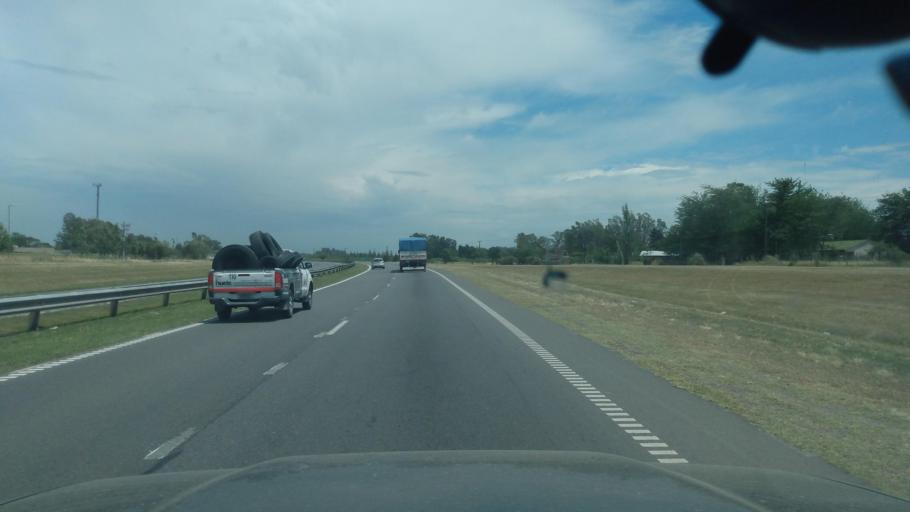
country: AR
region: Buenos Aires
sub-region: Partido de Lujan
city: Lujan
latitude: -34.5430
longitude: -59.1334
